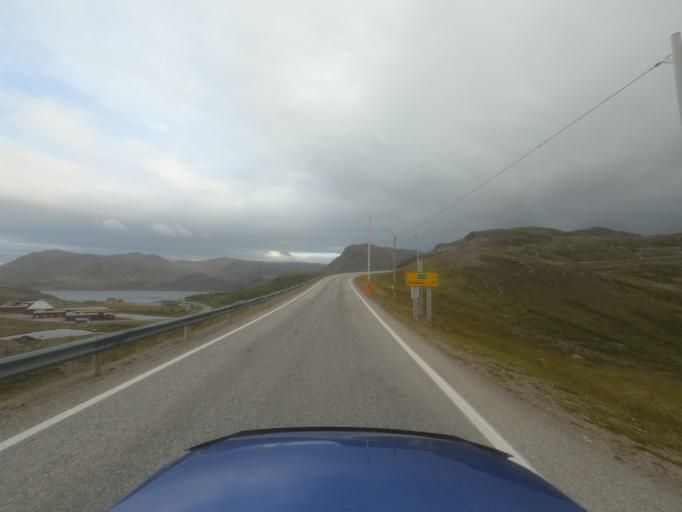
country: NO
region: Finnmark Fylke
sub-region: Nordkapp
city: Honningsvag
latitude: 71.0325
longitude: 25.8855
